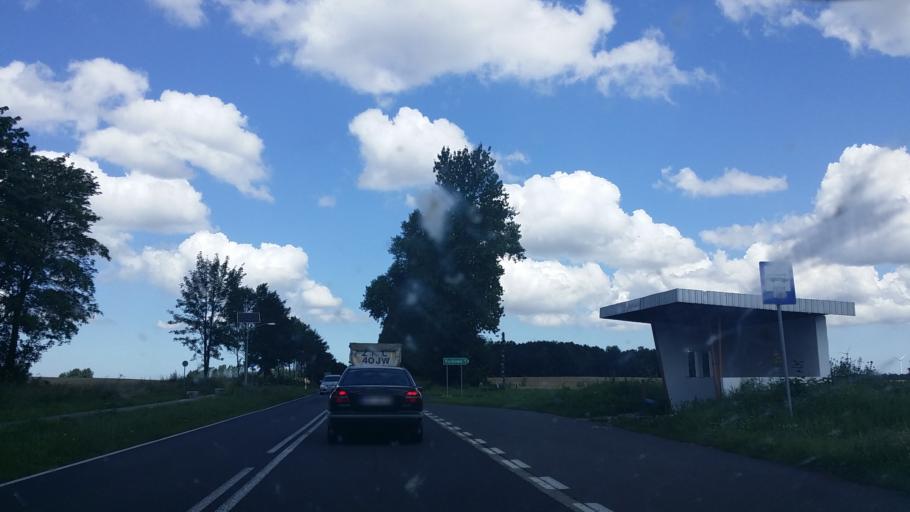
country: PL
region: West Pomeranian Voivodeship
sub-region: Powiat kolobrzeski
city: Goscino
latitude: 54.0182
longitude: 15.6602
